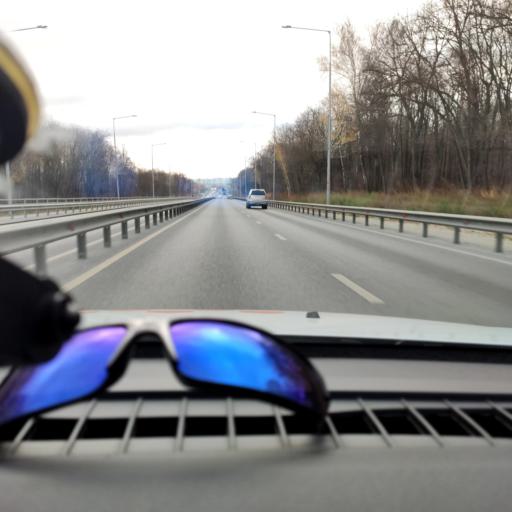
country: RU
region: Samara
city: Volzhskiy
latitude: 53.3604
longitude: 50.2052
